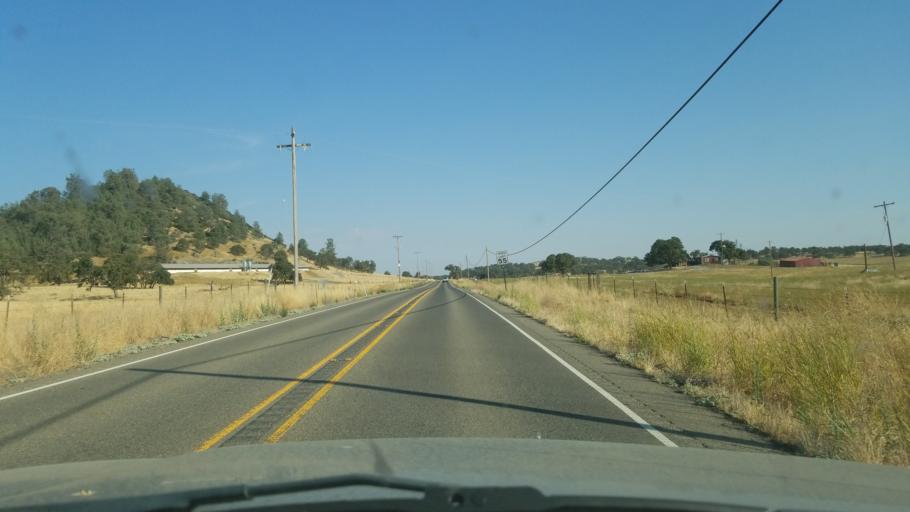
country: US
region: California
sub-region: Tuolumne County
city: Jamestown
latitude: 37.8306
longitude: -120.4770
